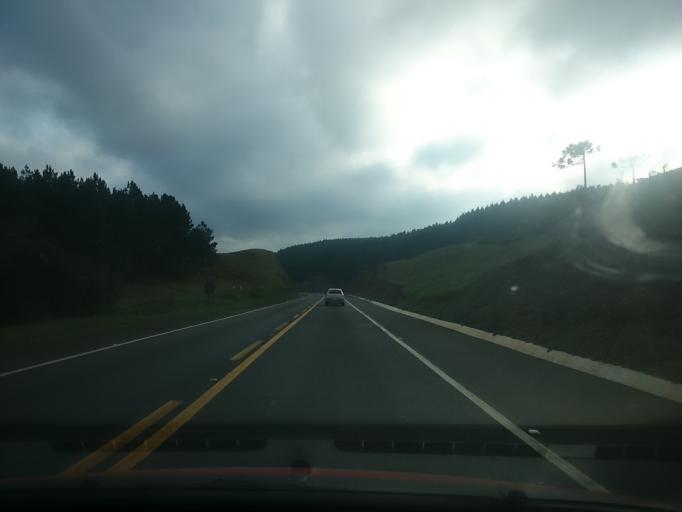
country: BR
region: Santa Catarina
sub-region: Lages
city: Lages
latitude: -27.9464
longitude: -50.4751
